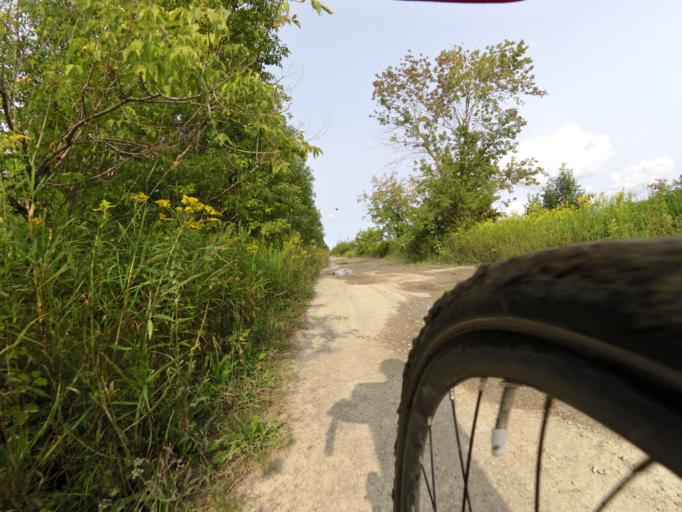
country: CA
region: Ontario
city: Quinte West
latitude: 44.0504
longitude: -77.6178
